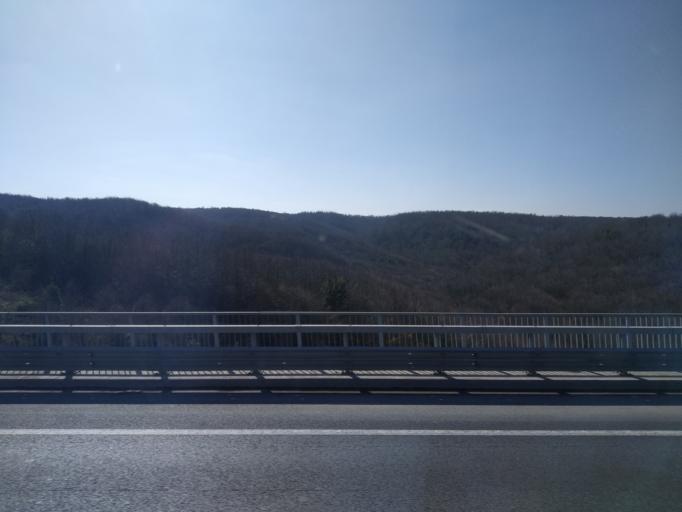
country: TR
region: Istanbul
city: Mahmut Sevket Pasa
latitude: 41.1692
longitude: 29.2501
